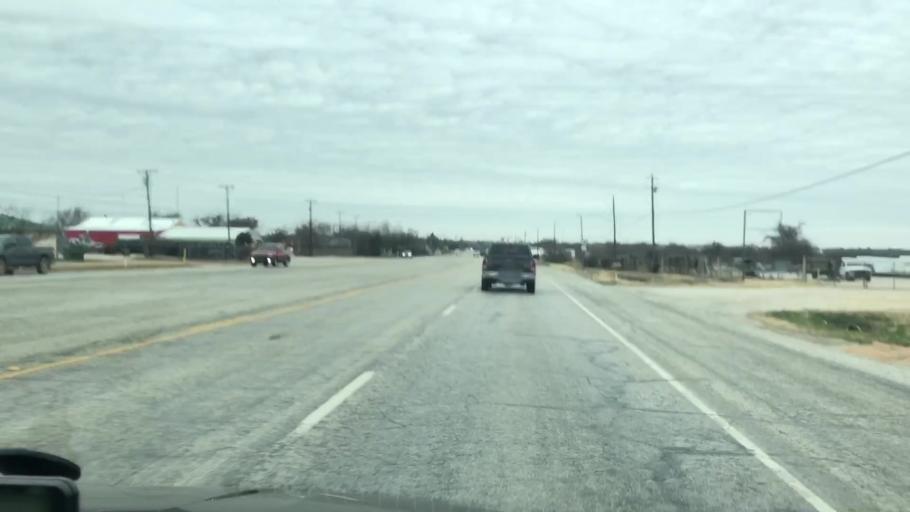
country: US
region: Texas
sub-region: Jack County
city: Jacksboro
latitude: 33.2035
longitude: -98.1516
